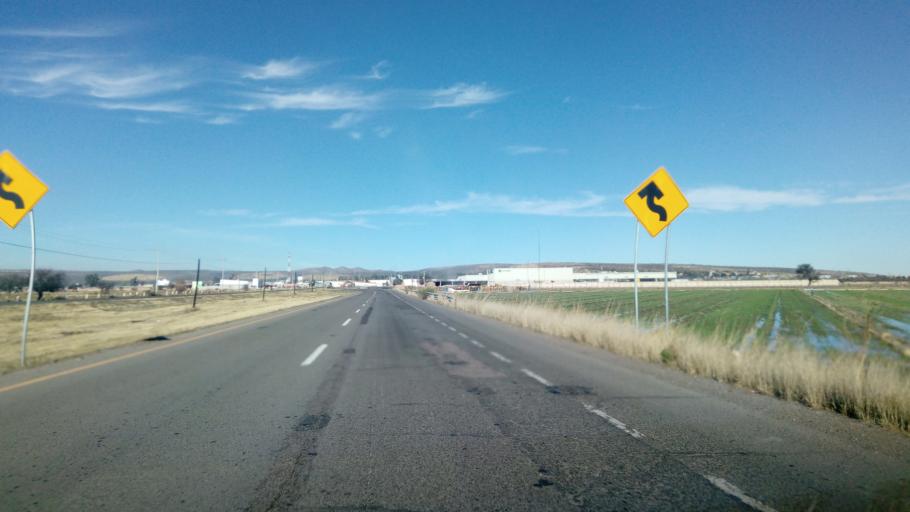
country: MX
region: Durango
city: Victoria de Durango
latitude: 24.0889
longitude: -104.5665
